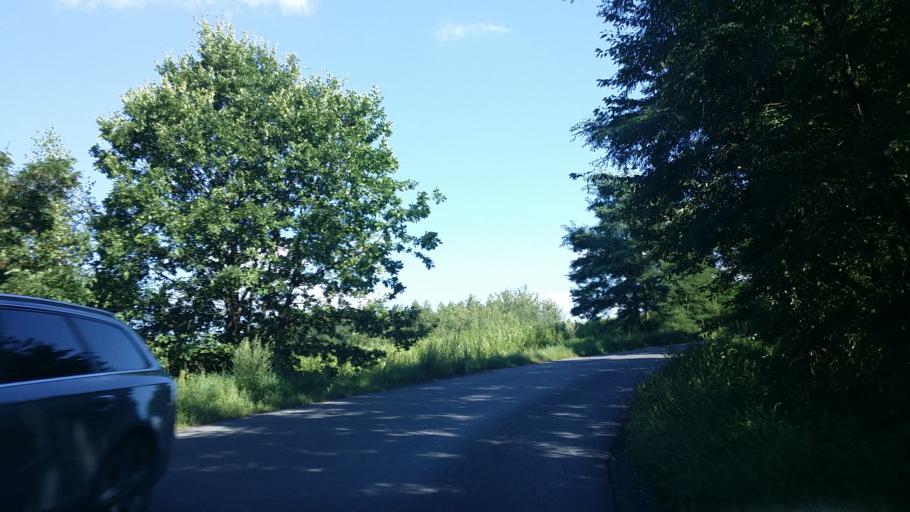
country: PL
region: Lesser Poland Voivodeship
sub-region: Powiat wadowicki
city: Wozniki
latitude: 49.9449
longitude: 19.4896
